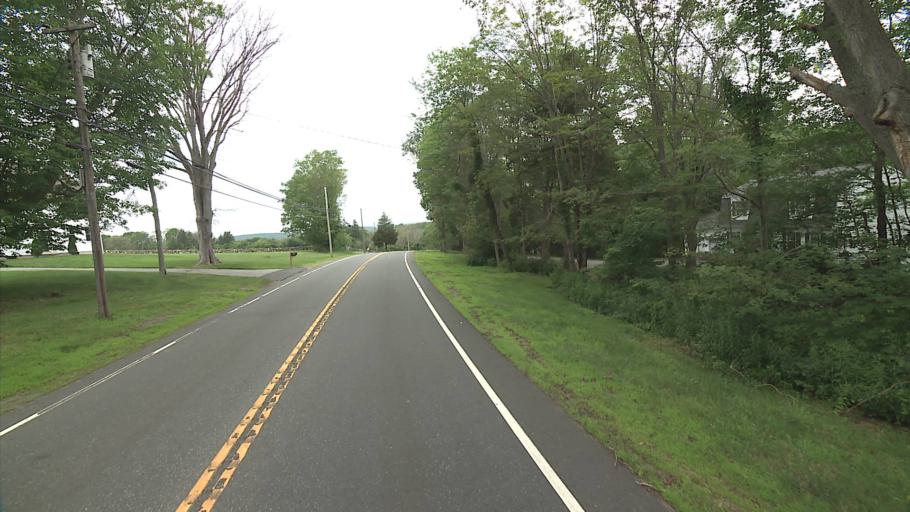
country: US
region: Connecticut
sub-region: New London County
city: Ledyard Center
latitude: 41.4676
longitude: -72.0240
